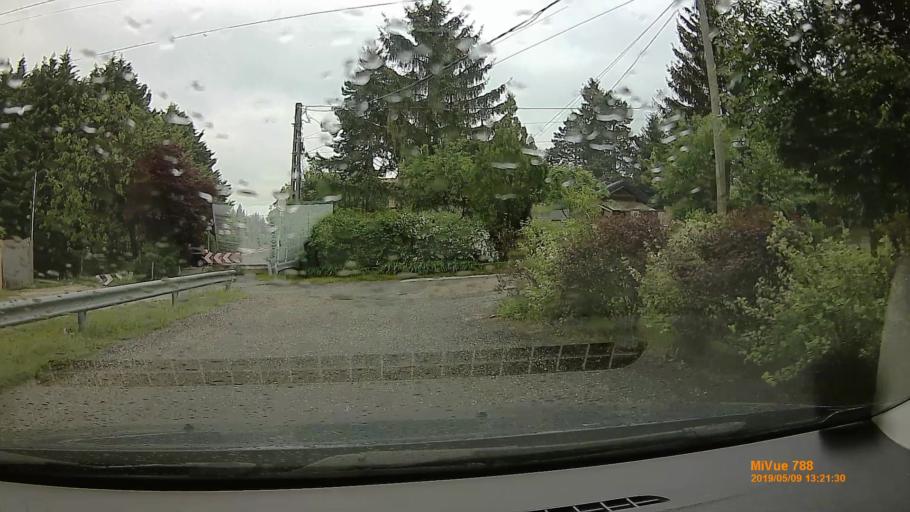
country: HU
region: Budapest
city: Budapest XVI. keruelet
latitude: 47.5391
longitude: 19.1901
